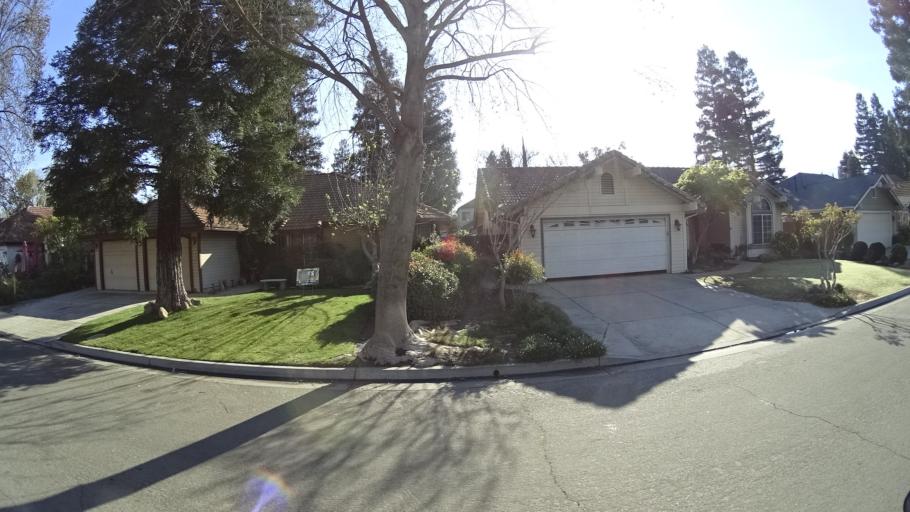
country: US
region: California
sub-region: Fresno County
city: West Park
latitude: 36.8284
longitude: -119.8591
